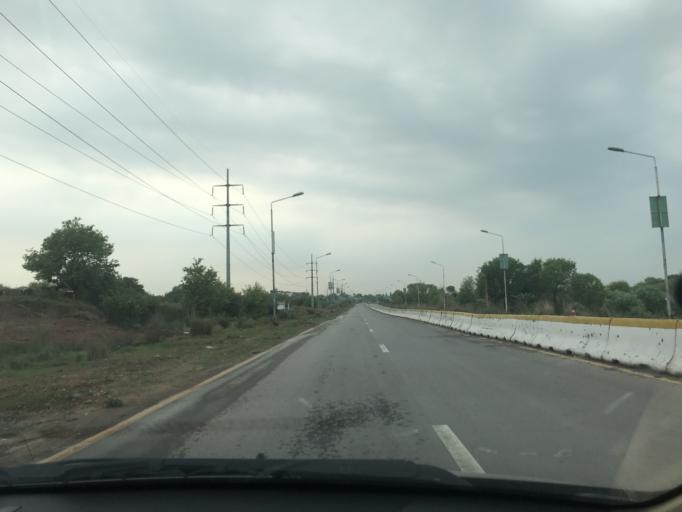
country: PK
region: Islamabad
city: Islamabad
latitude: 33.6980
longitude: 73.1817
